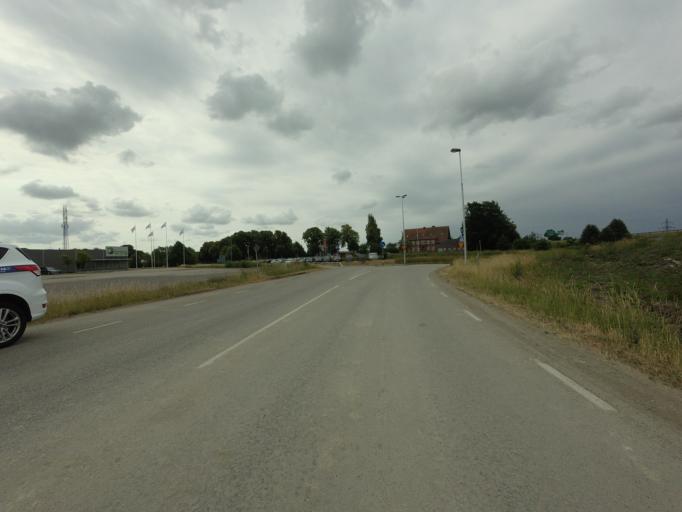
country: SE
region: Skane
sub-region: Lomma Kommun
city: Lomma
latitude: 55.6561
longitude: 13.0998
